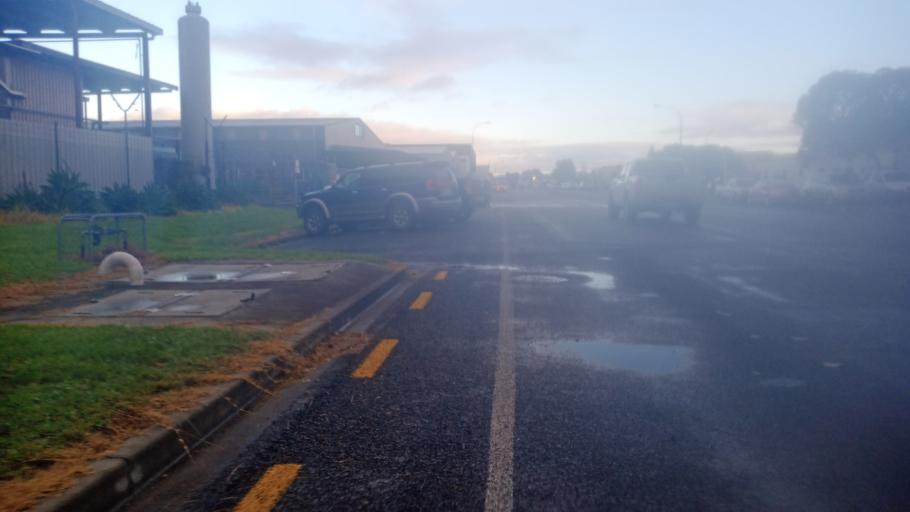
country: NZ
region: Gisborne
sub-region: Gisborne District
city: Gisborne
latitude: -38.6670
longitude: 177.9971
